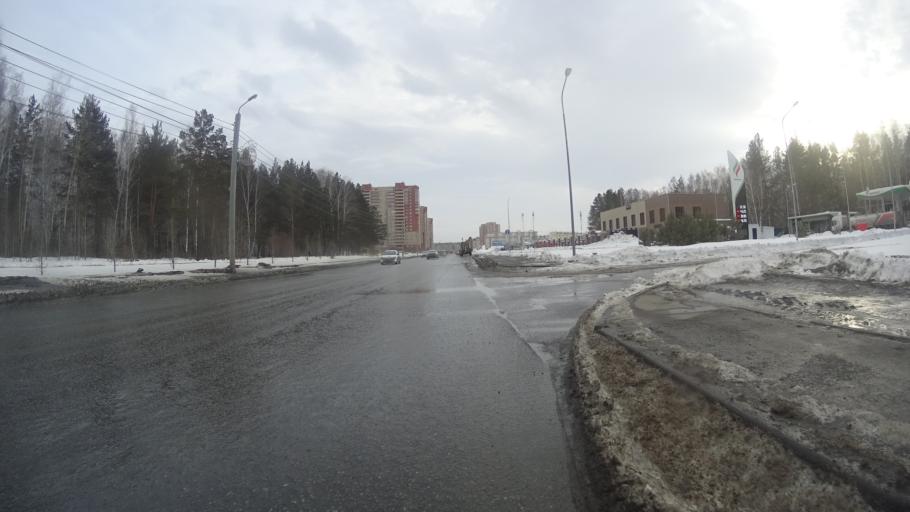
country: RU
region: Chelyabinsk
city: Roshchino
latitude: 55.1989
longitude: 61.2802
